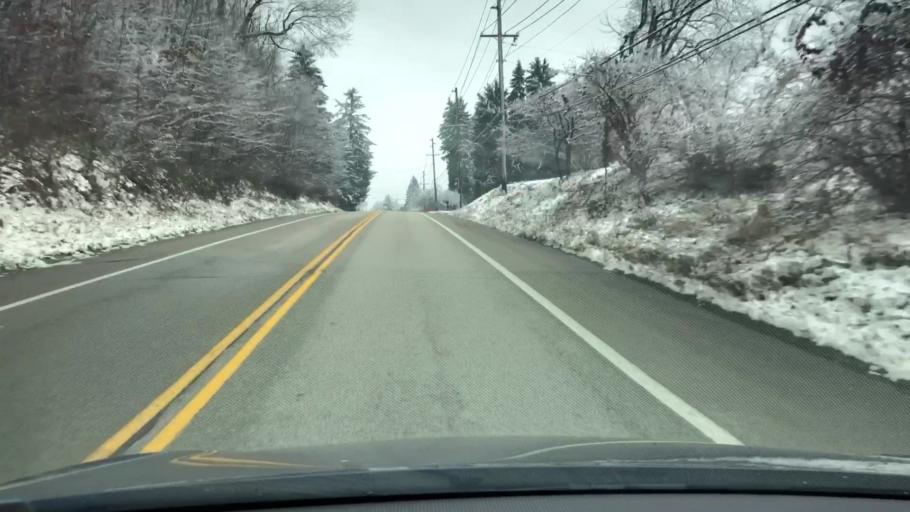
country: US
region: Pennsylvania
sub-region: Fayette County
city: Hopwood
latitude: 39.8212
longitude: -79.5906
